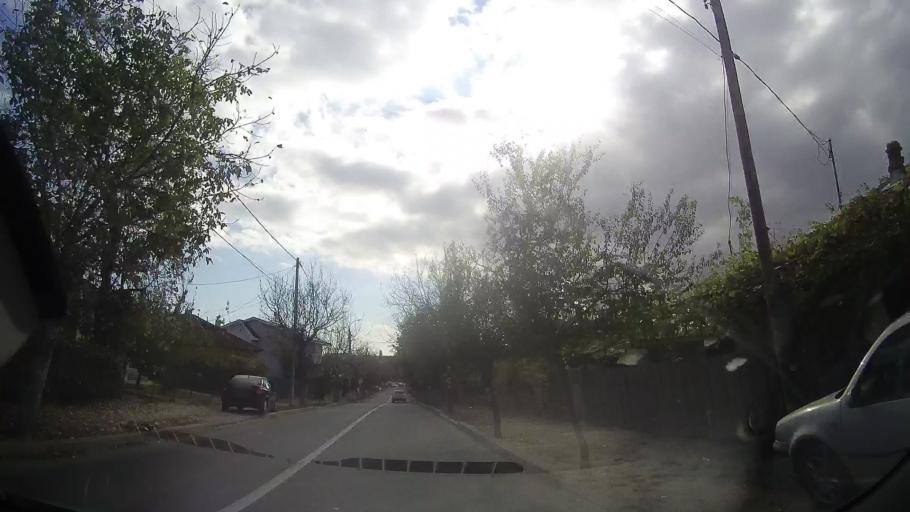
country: RO
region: Constanta
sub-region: Oras Techirghiol
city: Techirghiol
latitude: 44.0576
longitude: 28.6000
